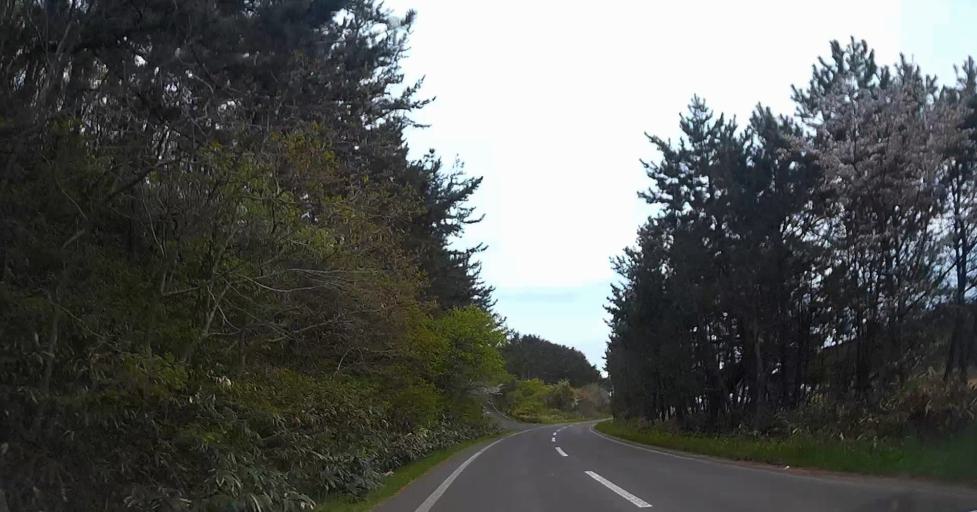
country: JP
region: Aomori
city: Shimokizukuri
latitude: 40.9380
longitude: 140.3176
